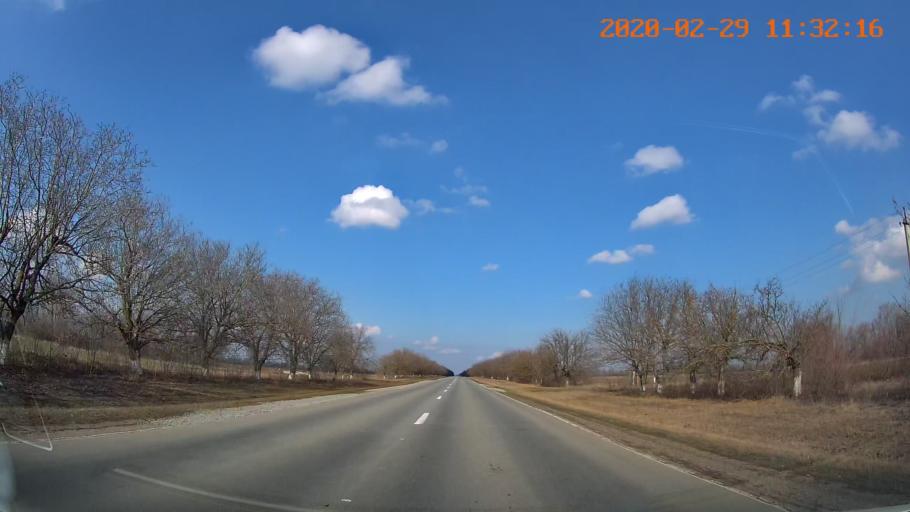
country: MD
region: Rezina
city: Saharna
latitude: 47.5356
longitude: 29.0962
